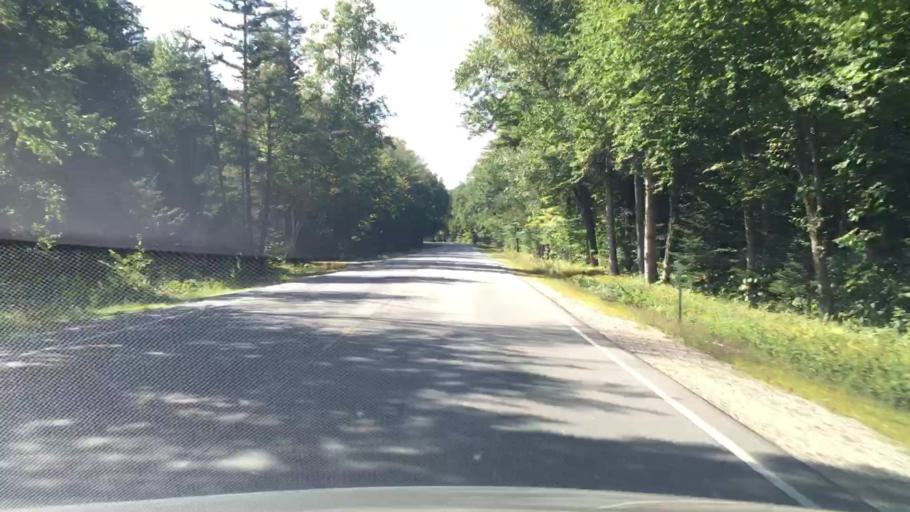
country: US
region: New Hampshire
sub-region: Carroll County
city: Tamworth
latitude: 43.9965
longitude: -71.3788
